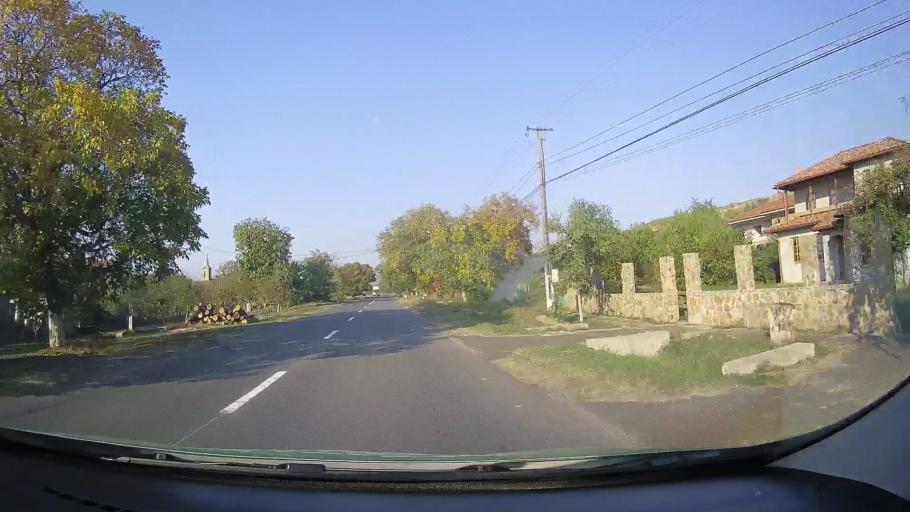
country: RO
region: Arad
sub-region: Comuna Paulis
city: Paulis
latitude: 46.1222
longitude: 21.5979
